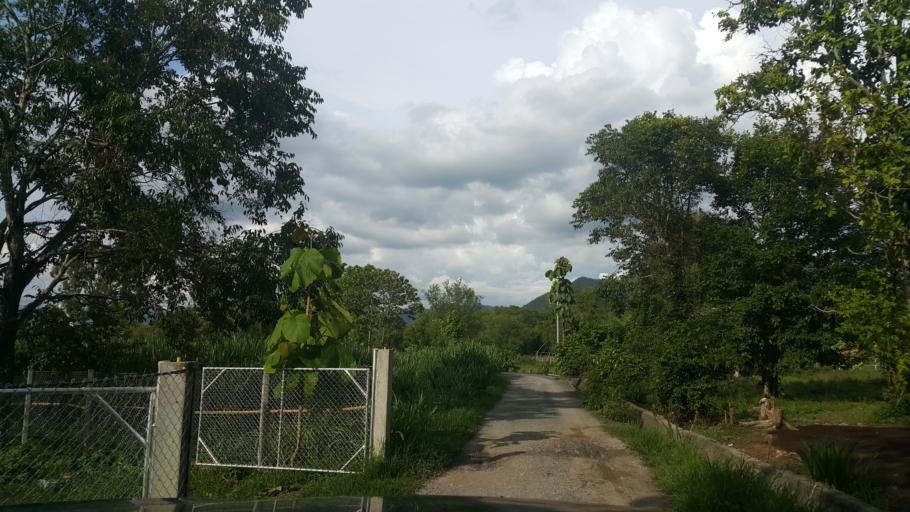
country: TH
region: Chiang Mai
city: Mae On
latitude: 18.7187
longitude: 99.2126
